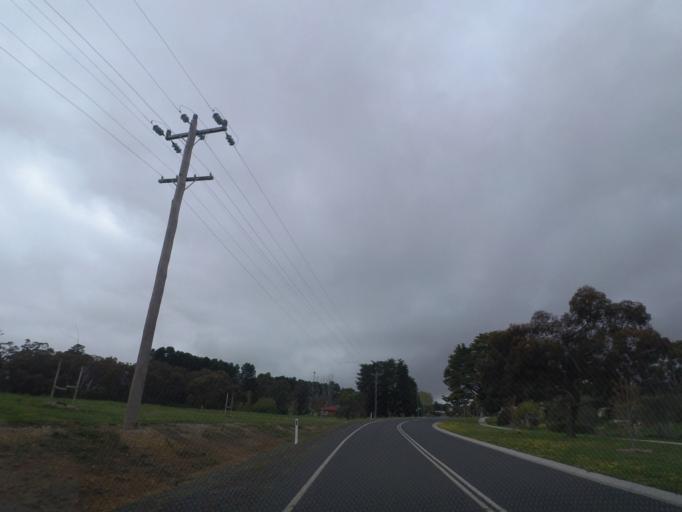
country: AU
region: Victoria
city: Brown Hill
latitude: -37.6247
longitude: 144.1047
